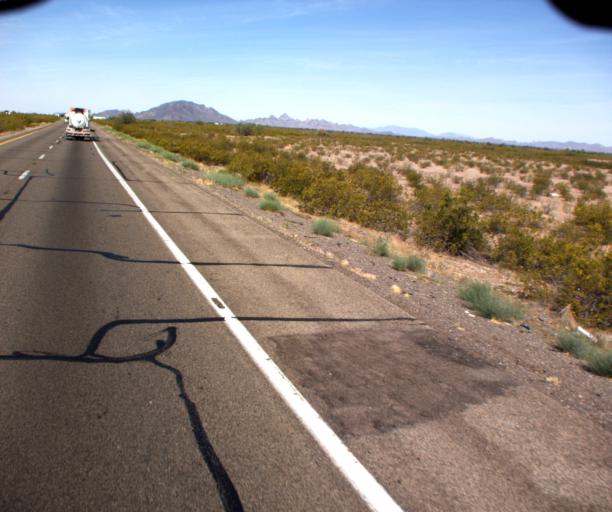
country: US
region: Arizona
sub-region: Maricopa County
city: Buckeye
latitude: 33.4998
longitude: -112.9473
